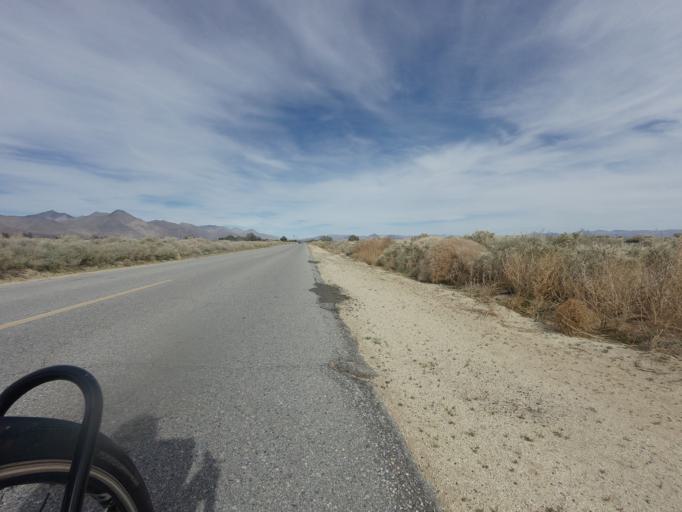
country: US
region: California
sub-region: Kern County
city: Inyokern
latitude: 35.7214
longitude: -117.8344
